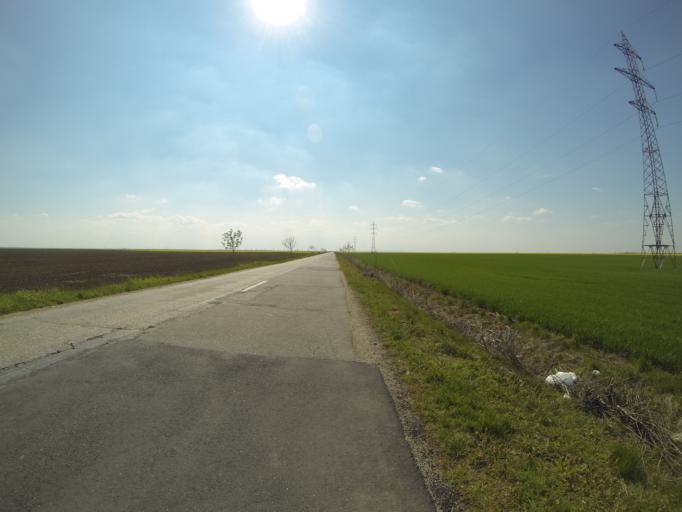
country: RO
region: Mehedinti
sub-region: Comuna Darvari
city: Gemeni
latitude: 44.1513
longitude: 23.1143
